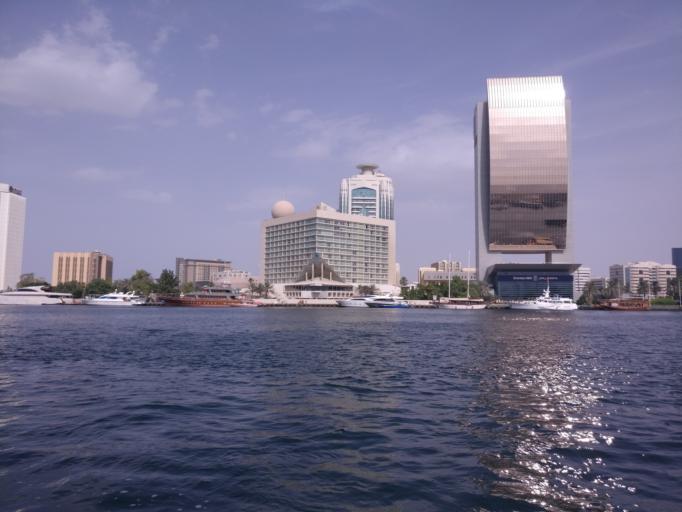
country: AE
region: Ash Shariqah
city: Sharjah
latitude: 25.2593
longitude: 55.3119
